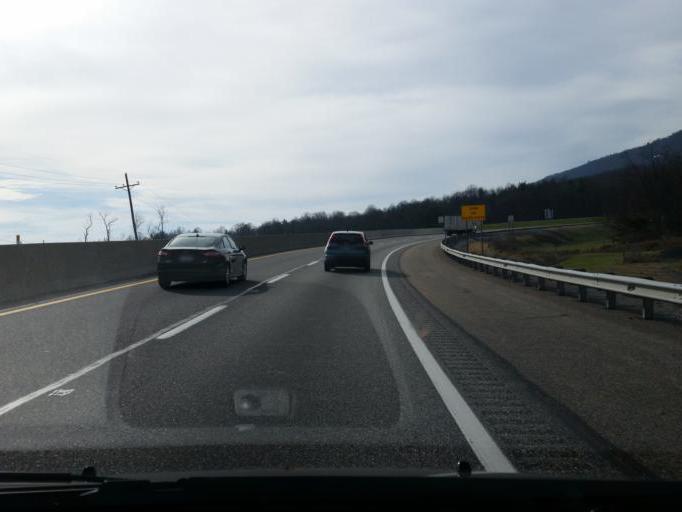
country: US
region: Pennsylvania
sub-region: Franklin County
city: Doylestown
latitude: 40.0887
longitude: -77.8270
